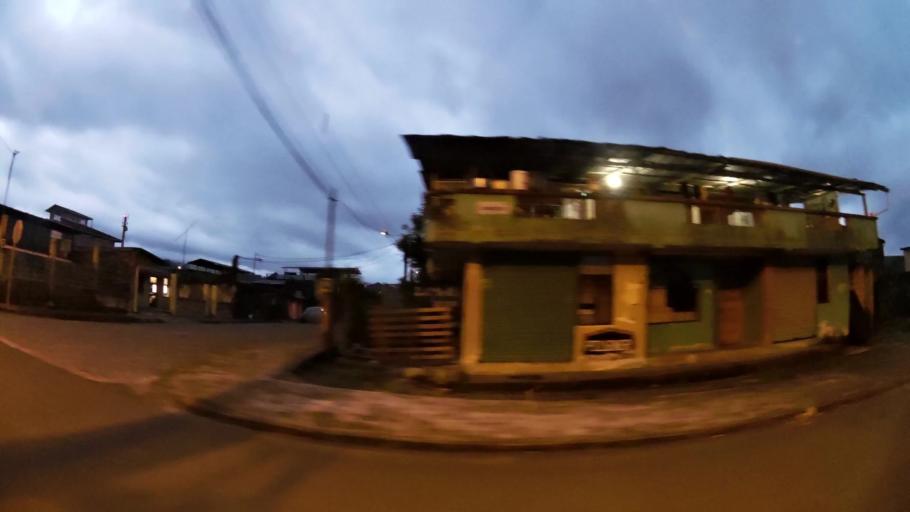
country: EC
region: Pastaza
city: Puyo
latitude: -1.4808
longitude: -78.0039
